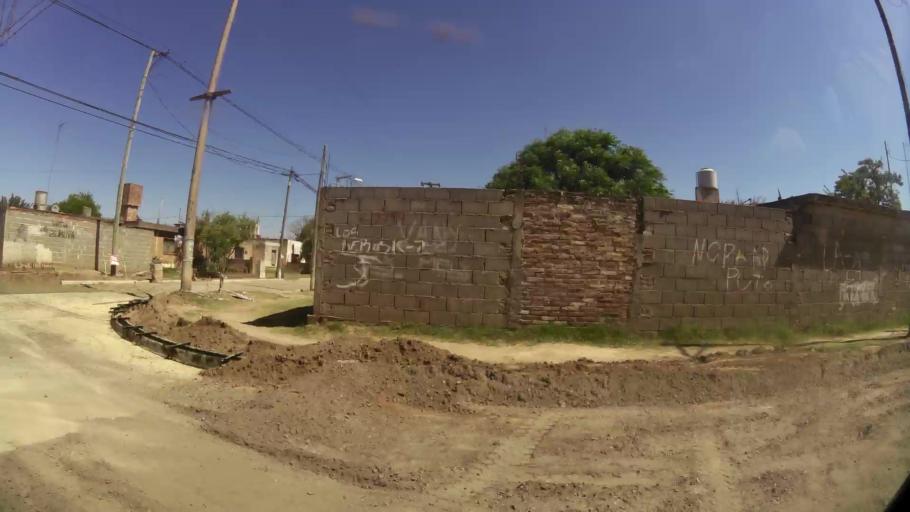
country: AR
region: Cordoba
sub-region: Departamento de Capital
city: Cordoba
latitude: -31.3707
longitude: -64.1315
